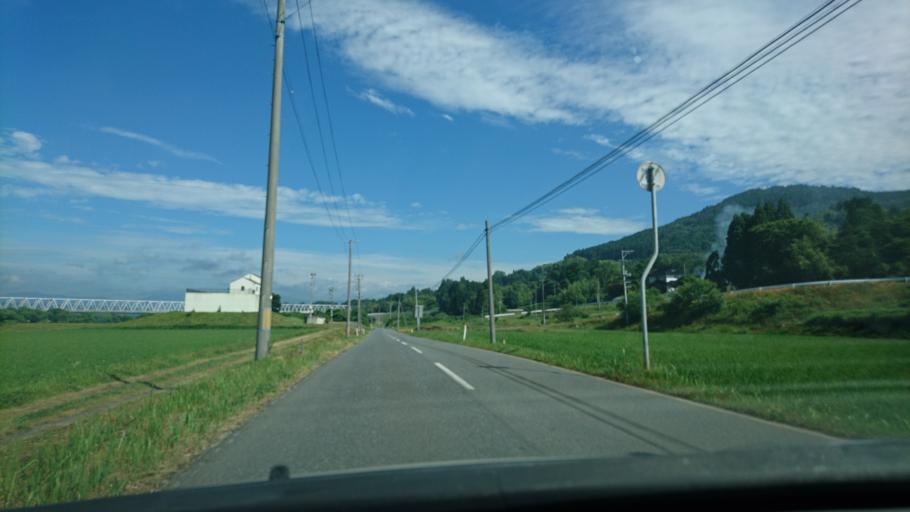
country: JP
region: Iwate
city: Ichinoseki
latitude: 38.9704
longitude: 141.1630
